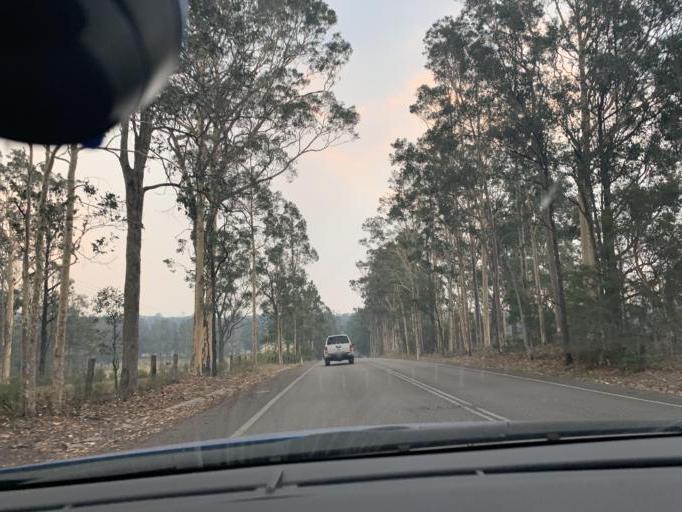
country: AU
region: New South Wales
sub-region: Cessnock
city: Cessnock
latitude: -32.9212
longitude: 151.3492
